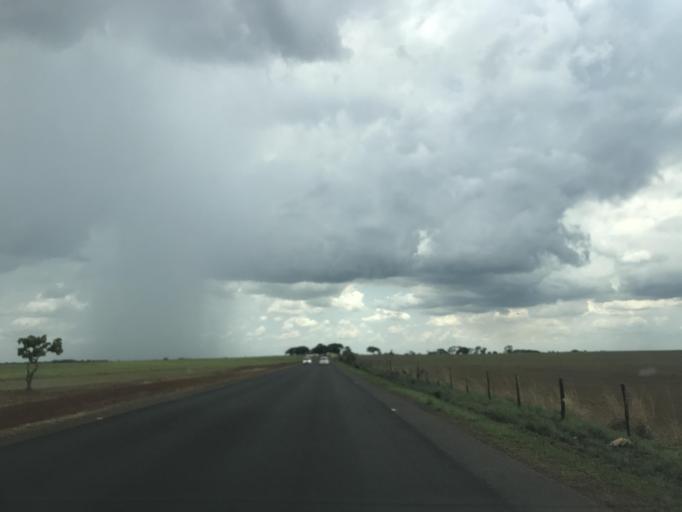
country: BR
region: Goias
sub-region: Vianopolis
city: Vianopolis
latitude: -16.8613
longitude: -48.5441
